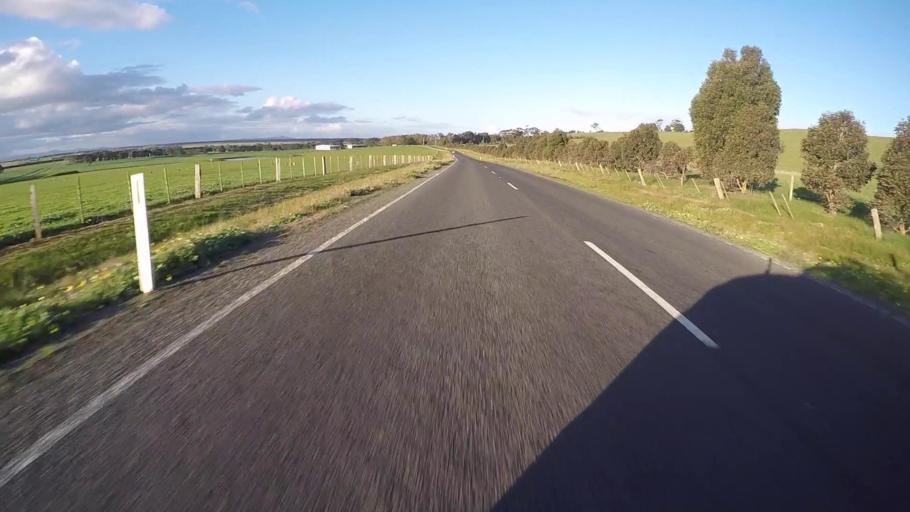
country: AU
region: Victoria
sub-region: Greater Geelong
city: Wandana Heights
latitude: -38.1537
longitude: 144.1698
